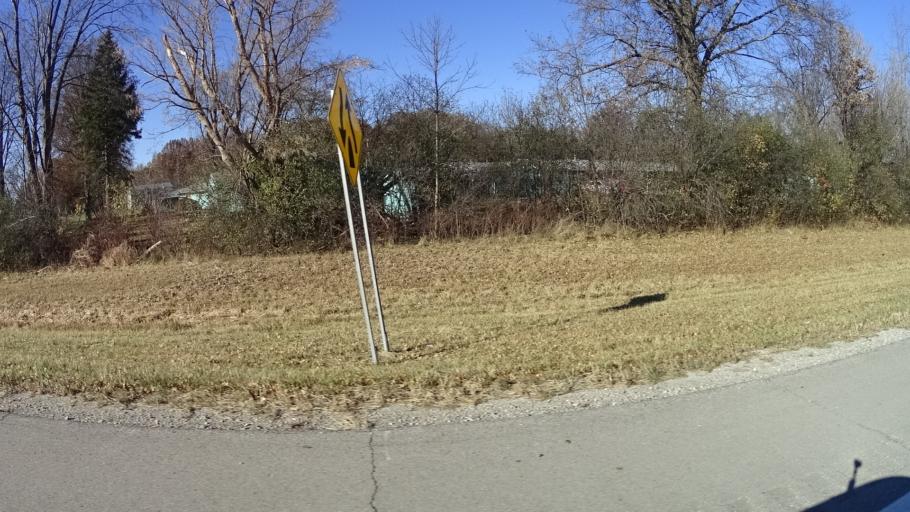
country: US
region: Ohio
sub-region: Lorain County
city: Oberlin
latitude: 41.2853
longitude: -82.1794
